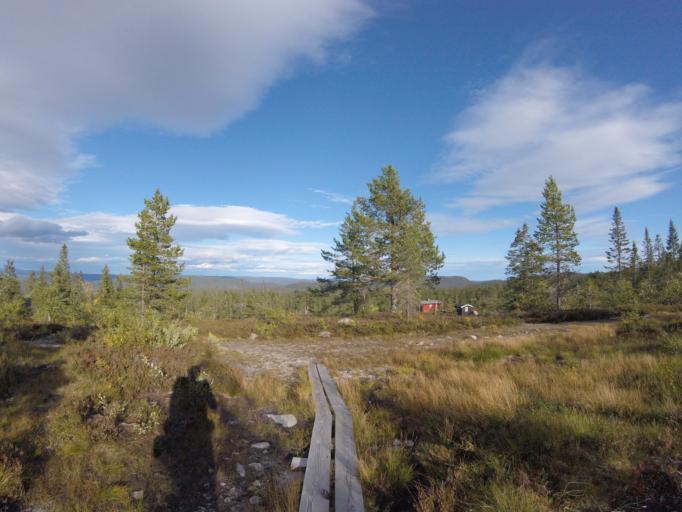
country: NO
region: Buskerud
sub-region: Flesberg
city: Lampeland
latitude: 59.7851
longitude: 9.4151
